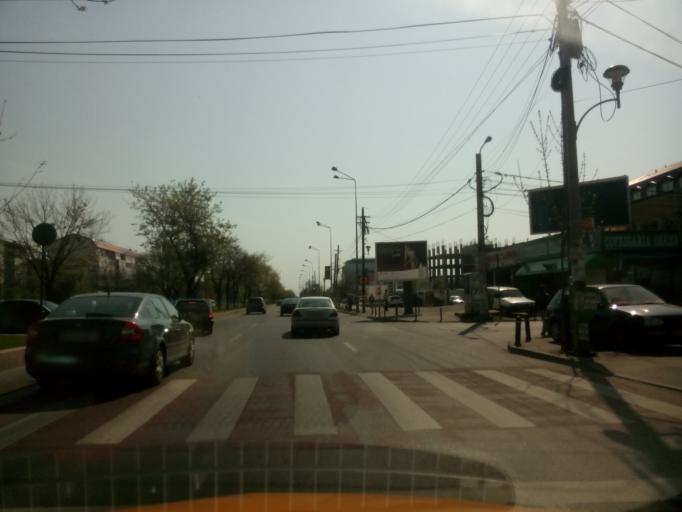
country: RO
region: Ilfov
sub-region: Comuna Popesti-Leordeni
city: Popesti-Leordeni
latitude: 44.4100
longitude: 26.1775
